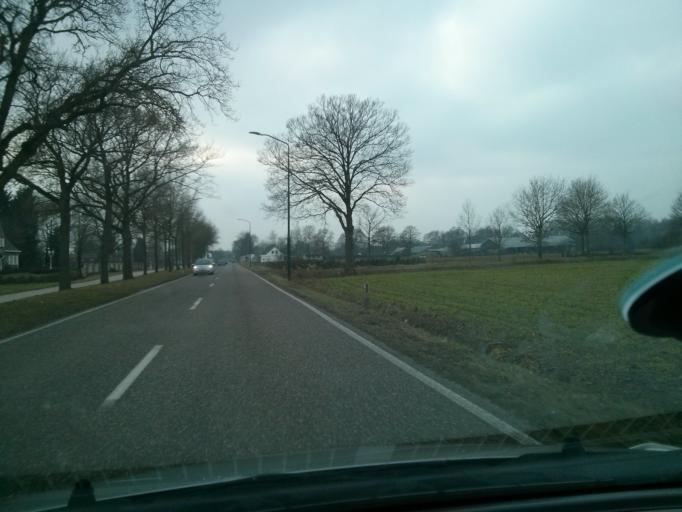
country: NL
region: North Brabant
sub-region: Gemeente Heeze-Leende
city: Heeze
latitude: 51.3745
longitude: 5.5948
